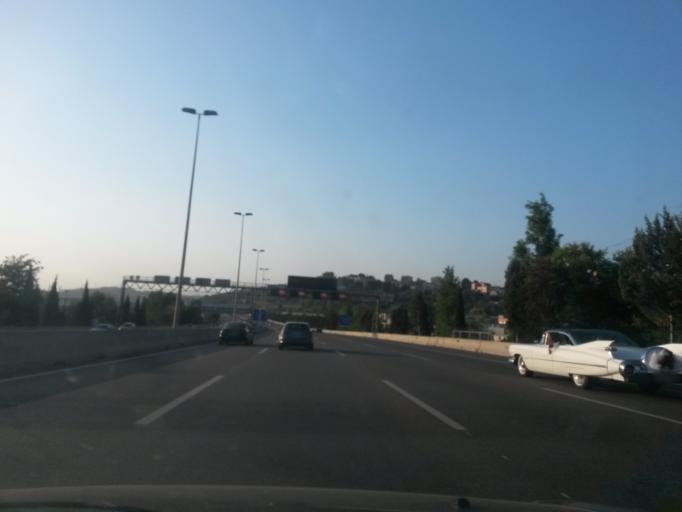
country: ES
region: Catalonia
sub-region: Provincia de Barcelona
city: Palleja
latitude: 41.4295
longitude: 2.0056
